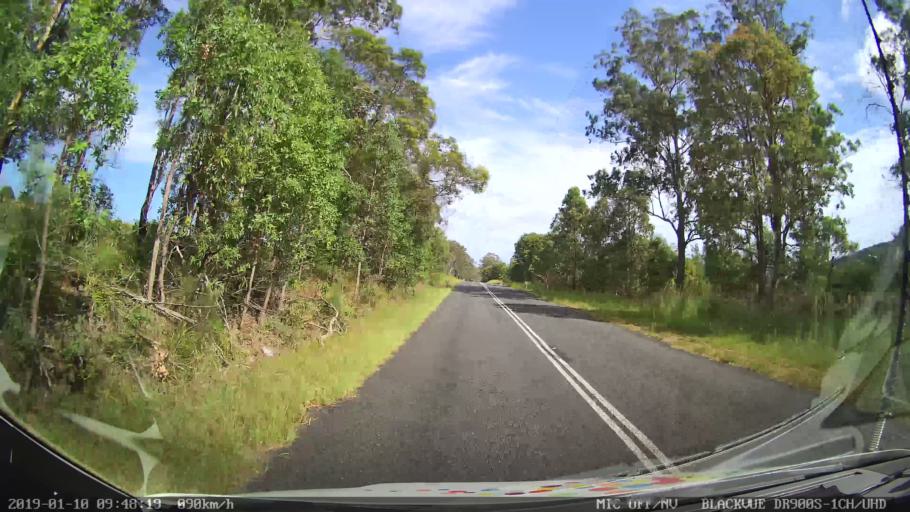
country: AU
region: New South Wales
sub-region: Coffs Harbour
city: Nana Glen
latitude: -30.0739
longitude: 152.9886
